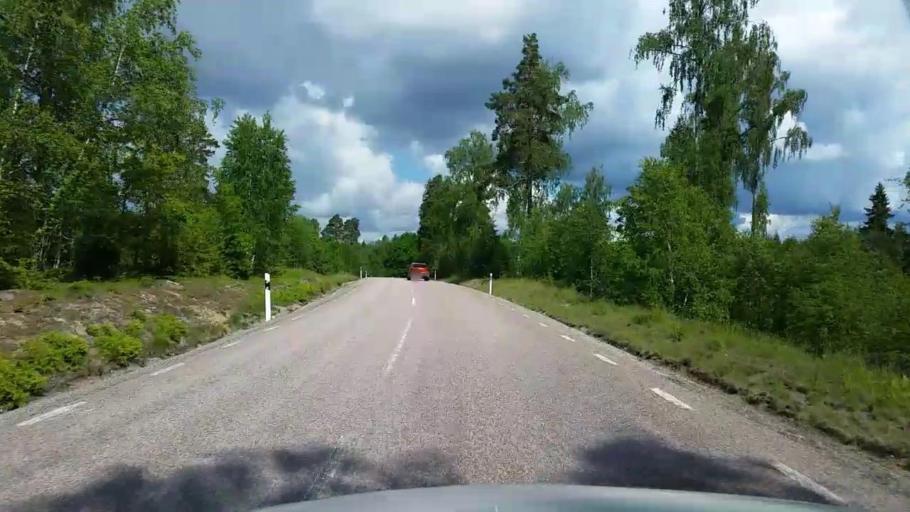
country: SE
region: Vaestmanland
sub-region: Skinnskattebergs Kommun
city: Skinnskatteberg
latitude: 59.7860
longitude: 15.8594
